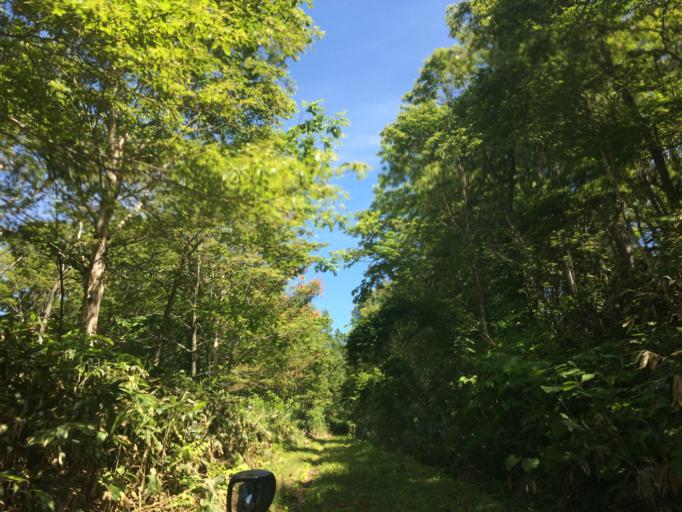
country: JP
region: Hokkaido
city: Niseko Town
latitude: 42.8569
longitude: 140.8185
